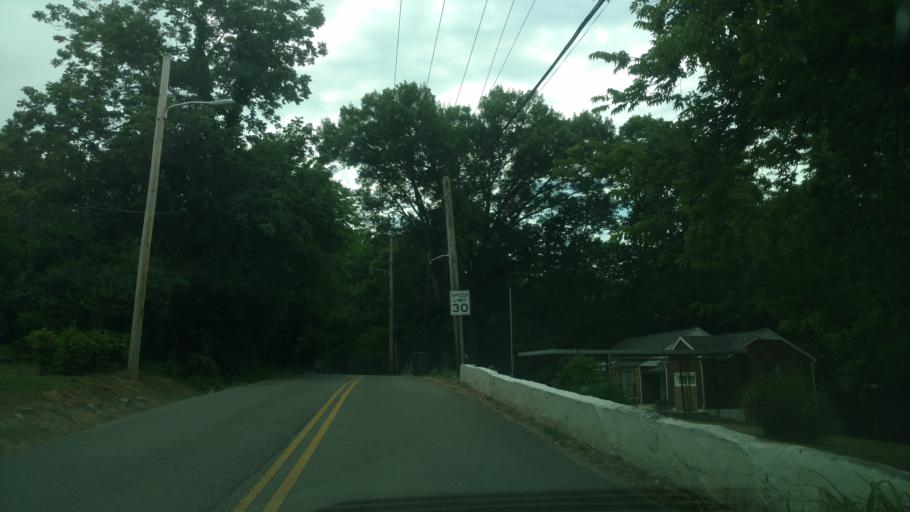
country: US
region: Tennessee
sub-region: Davidson County
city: Lakewood
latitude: 36.2175
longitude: -86.7085
